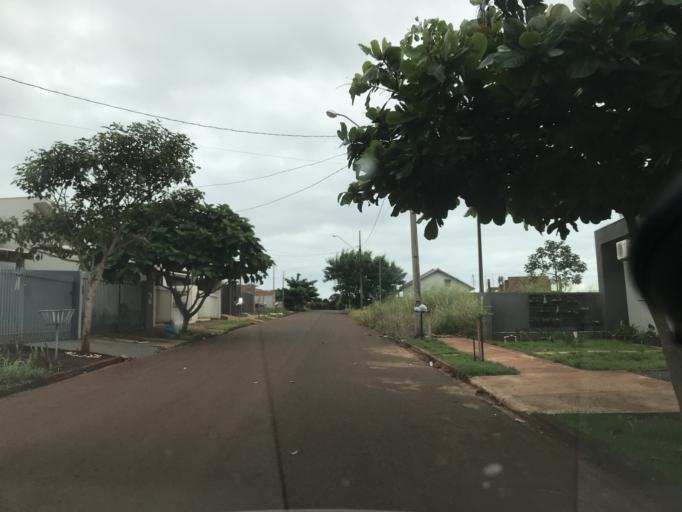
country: BR
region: Parana
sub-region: Palotina
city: Palotina
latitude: -24.2970
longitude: -53.8287
